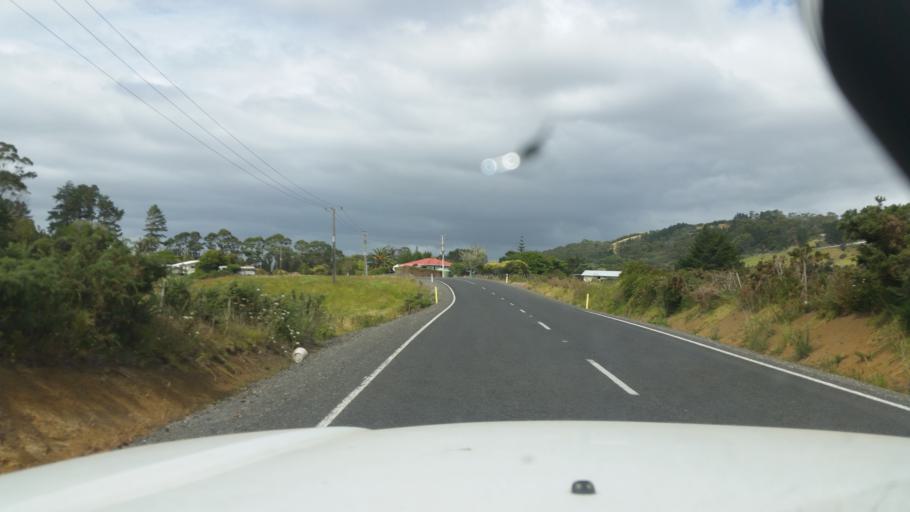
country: NZ
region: Northland
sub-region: Far North District
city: Ahipara
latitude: -35.1760
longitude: 173.1762
